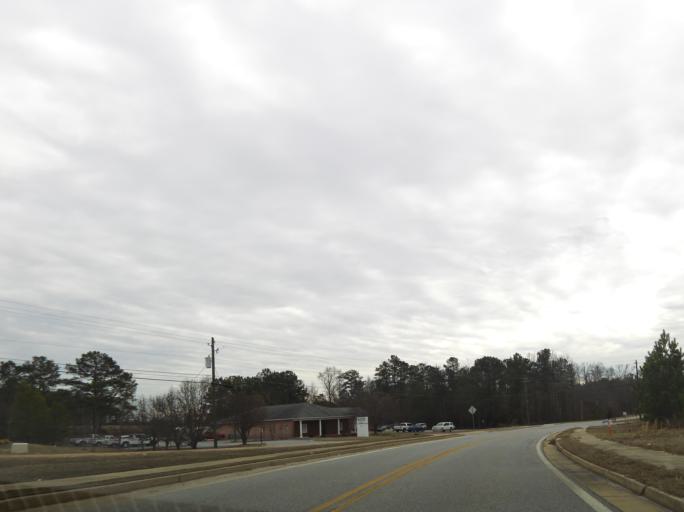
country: US
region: Georgia
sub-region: Bibb County
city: West Point
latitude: 32.8302
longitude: -83.7338
